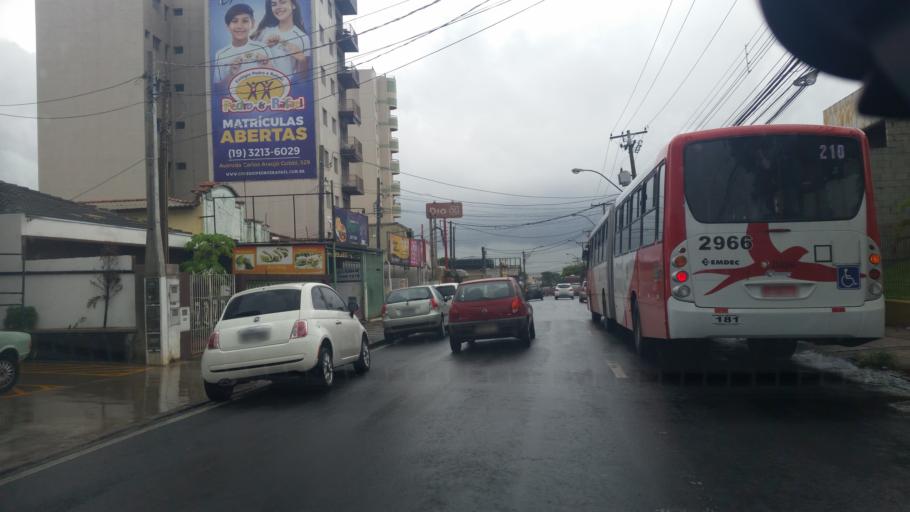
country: BR
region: Sao Paulo
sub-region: Campinas
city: Campinas
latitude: -22.9063
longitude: -47.0845
